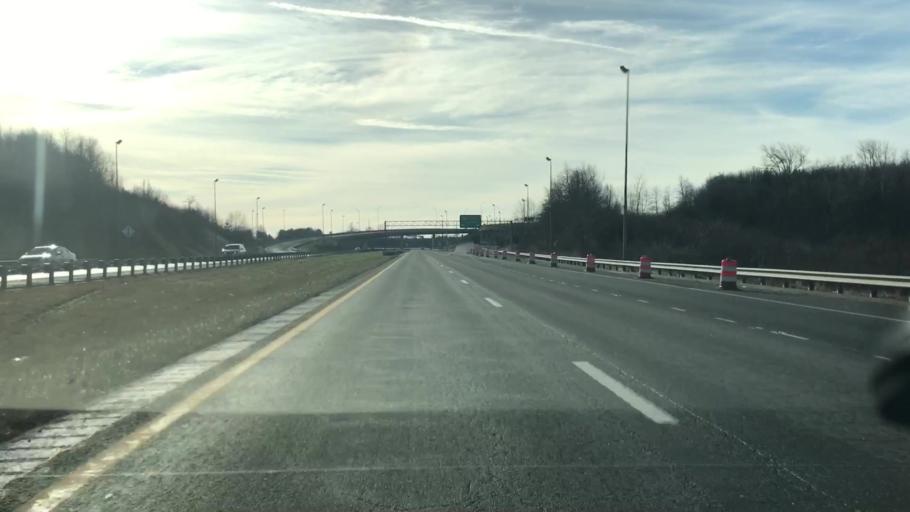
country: US
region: Virginia
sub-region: Montgomery County
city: Christiansburg
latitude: 37.1602
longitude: -80.4135
